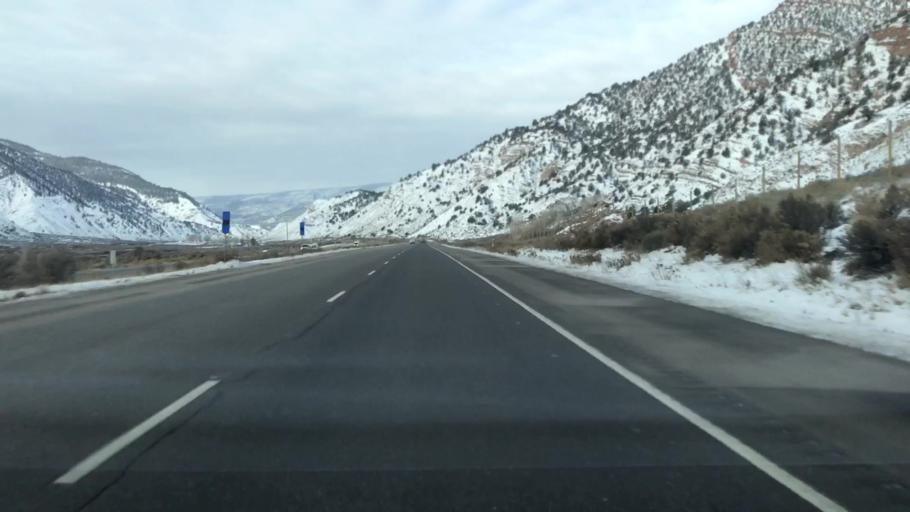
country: US
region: Colorado
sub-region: Eagle County
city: Gypsum
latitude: 39.6490
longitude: -107.0011
